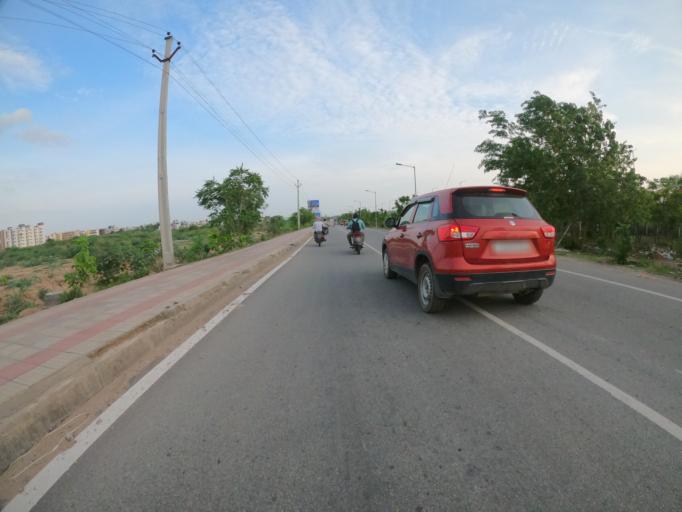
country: IN
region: Telangana
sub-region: Hyderabad
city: Hyderabad
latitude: 17.3943
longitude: 78.3526
